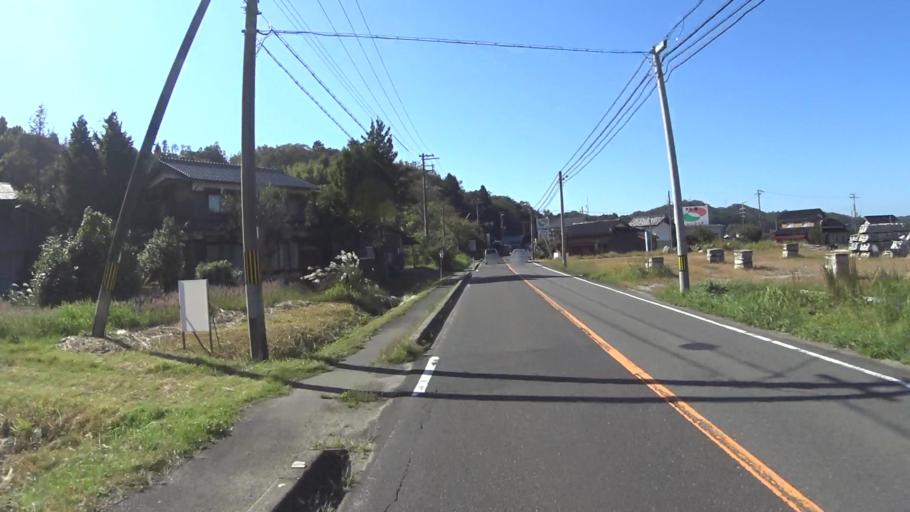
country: JP
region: Hyogo
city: Toyooka
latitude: 35.5805
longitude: 134.9674
